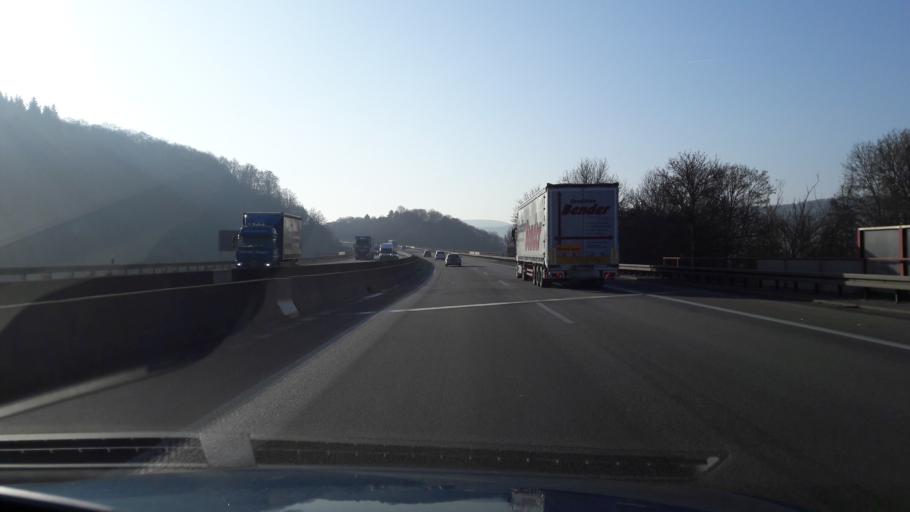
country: DE
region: Hesse
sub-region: Regierungsbezirk Giessen
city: Sinn
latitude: 50.6412
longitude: 8.3250
